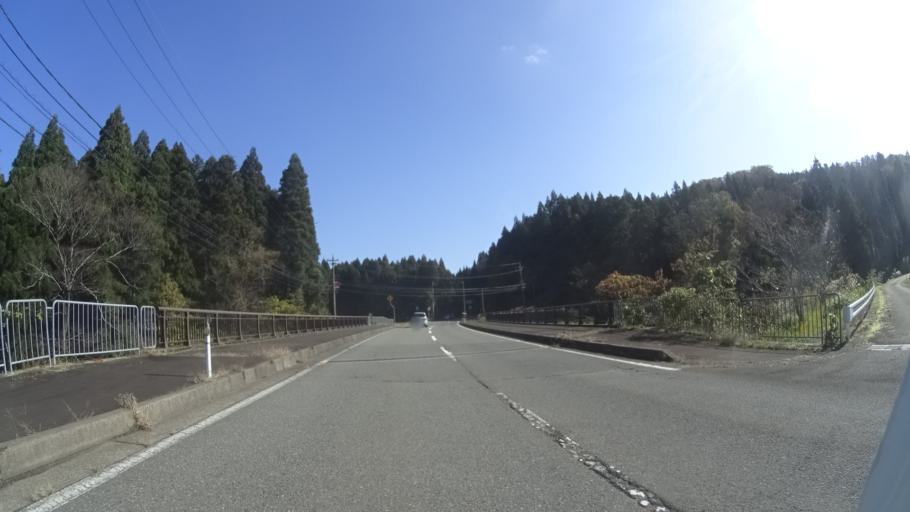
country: JP
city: Asahi
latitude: 35.9660
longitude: 136.0994
